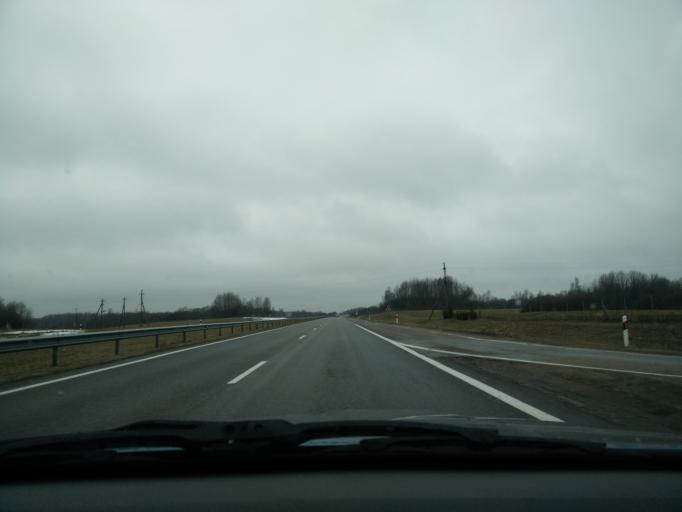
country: LT
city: Silale
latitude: 55.5363
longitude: 22.3119
